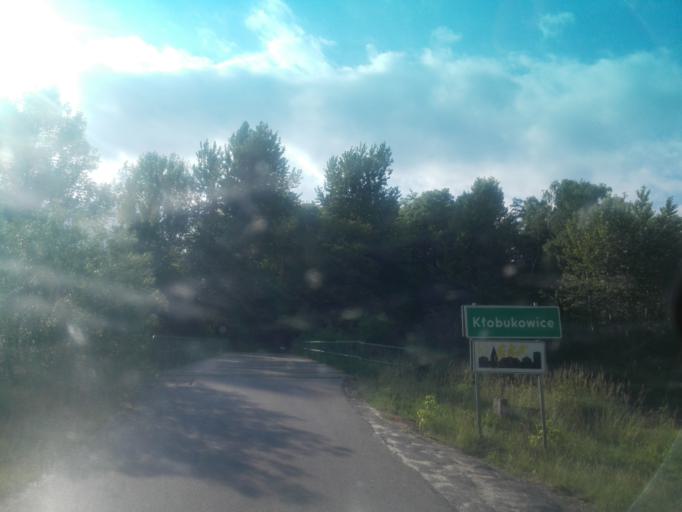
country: PL
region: Silesian Voivodeship
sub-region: Powiat czestochowski
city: Mstow
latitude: 50.8386
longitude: 19.3269
